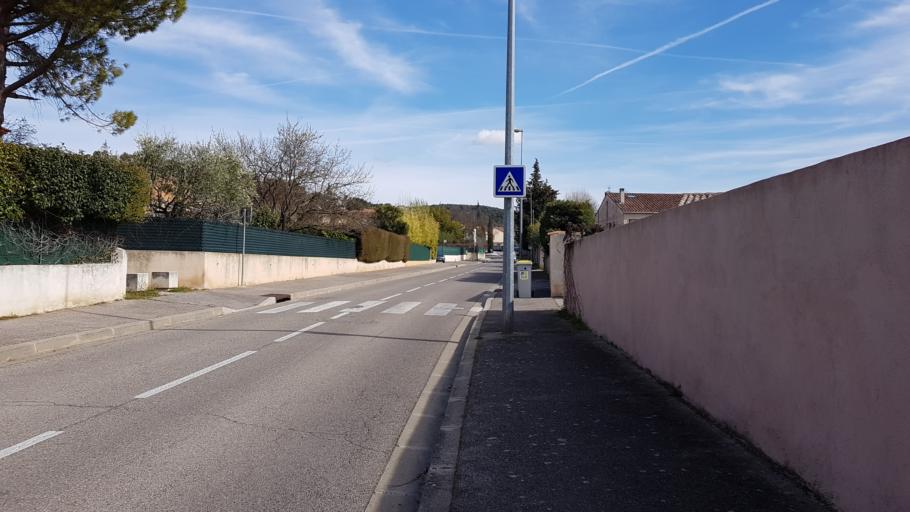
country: FR
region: Provence-Alpes-Cote d'Azur
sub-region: Departement des Bouches-du-Rhone
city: Bouc-Bel-Air
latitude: 43.4874
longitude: 5.4197
